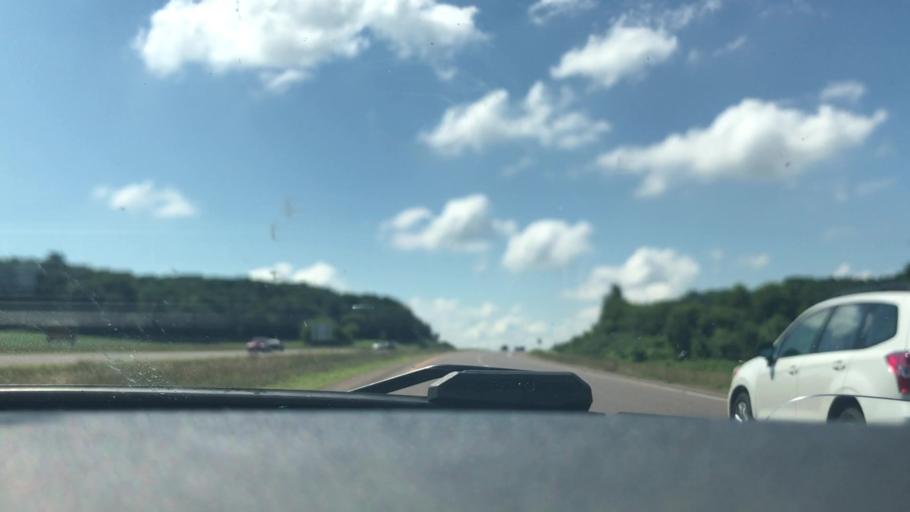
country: US
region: Wisconsin
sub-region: Chippewa County
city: Chippewa Falls
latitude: 44.9600
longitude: -91.4254
